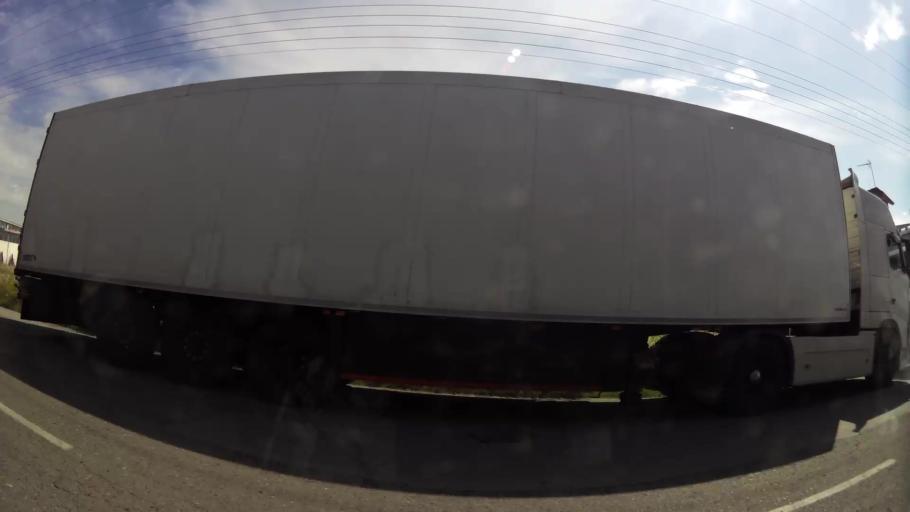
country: GR
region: Central Macedonia
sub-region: Nomos Pierias
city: Katerini
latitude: 40.2797
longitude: 22.4893
